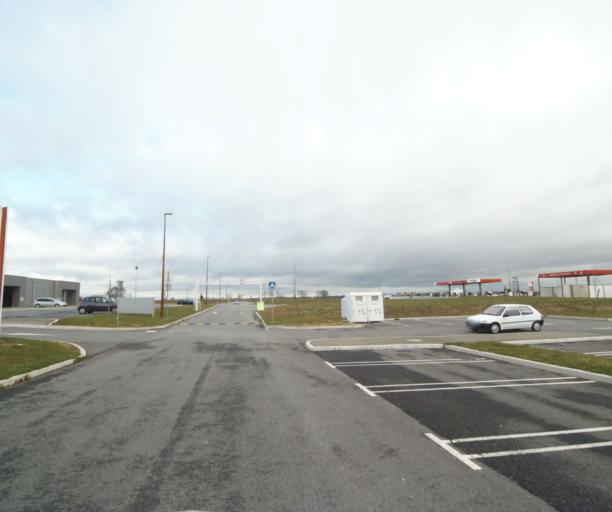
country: FR
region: Midi-Pyrenees
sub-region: Departement de l'Ariege
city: Saverdun
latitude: 43.2512
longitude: 1.5647
